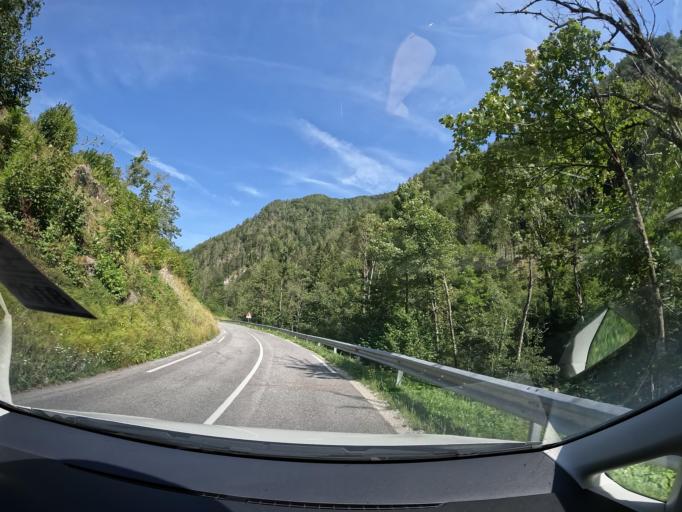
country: SI
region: Zirovnica
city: Zirovnica
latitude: 46.4426
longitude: 14.1513
